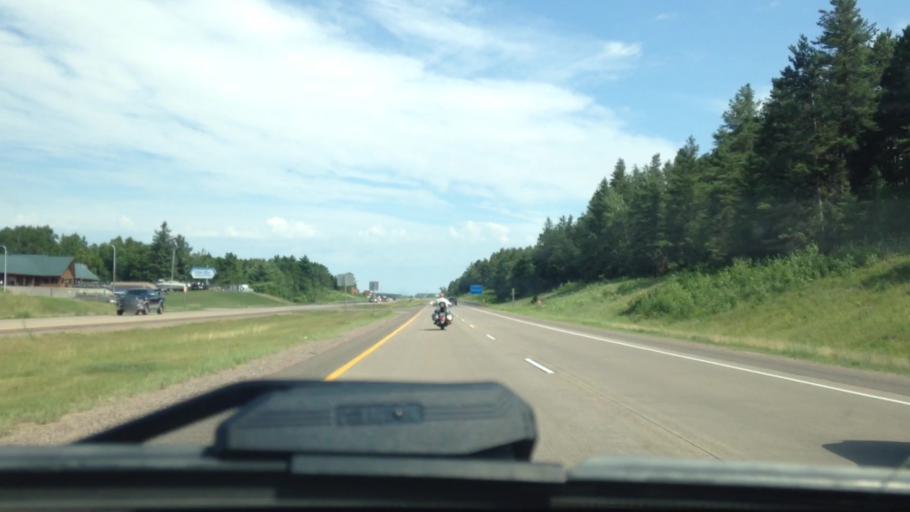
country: US
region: Wisconsin
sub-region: Washburn County
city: Spooner
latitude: 45.8894
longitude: -91.8277
